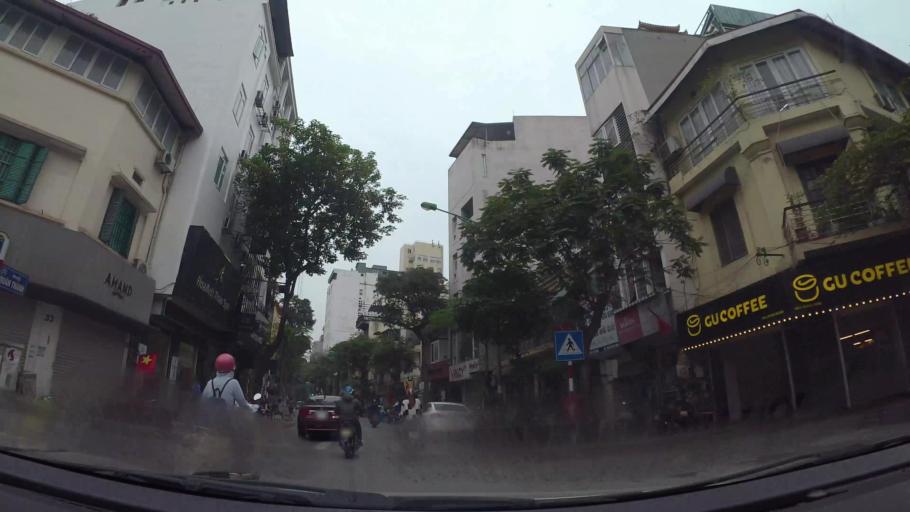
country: VN
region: Ha Noi
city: Hoan Kiem
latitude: 21.0420
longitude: 105.8439
